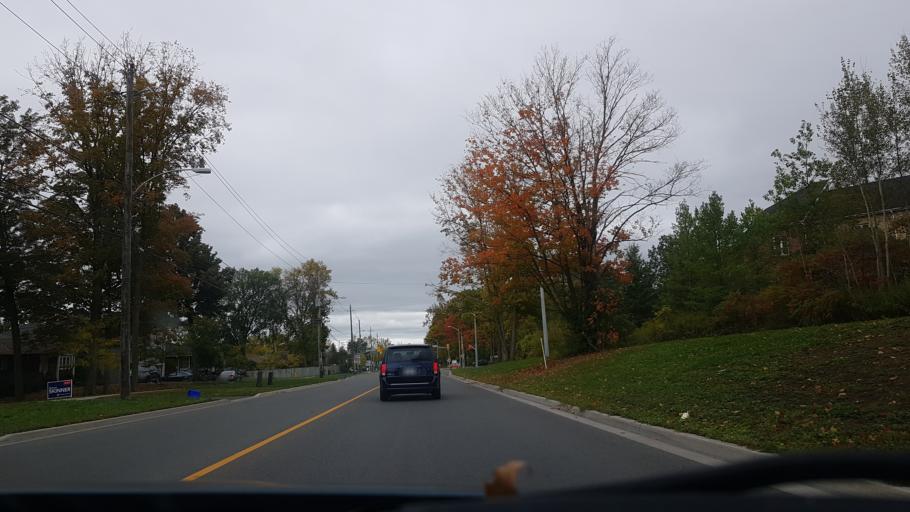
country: CA
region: Ontario
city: Peterborough
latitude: 44.2686
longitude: -78.3688
